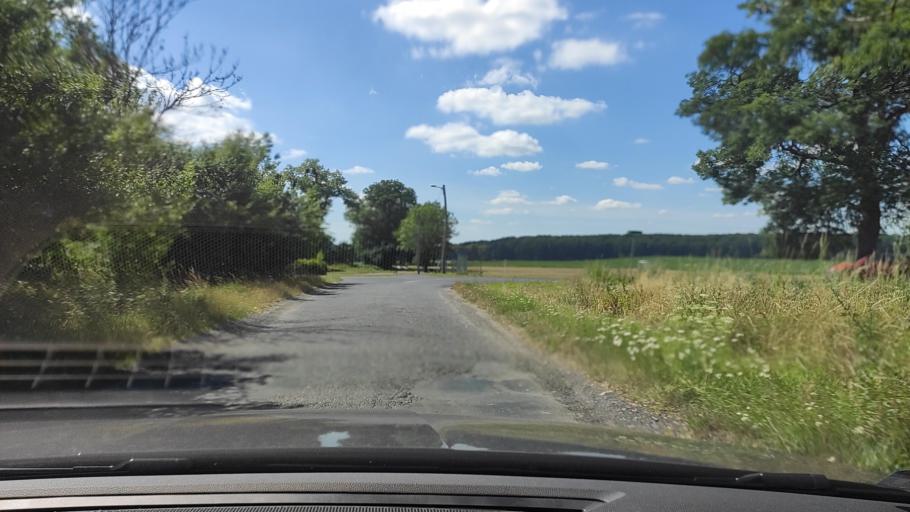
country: PL
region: Greater Poland Voivodeship
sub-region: Powiat poznanski
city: Kobylnica
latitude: 52.4975
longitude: 17.1078
